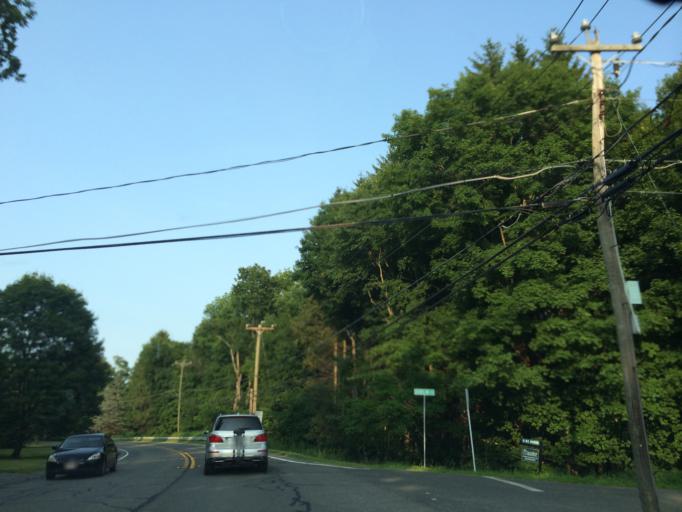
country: US
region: Massachusetts
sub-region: Berkshire County
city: Richmond
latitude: 42.4068
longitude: -73.3538
